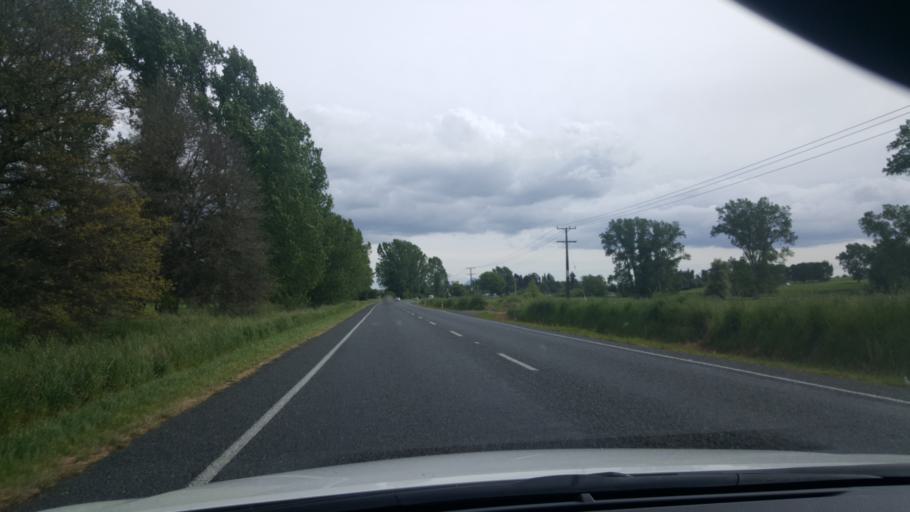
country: NZ
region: Waikato
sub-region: Taupo District
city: Taupo
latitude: -38.4616
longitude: 176.3154
